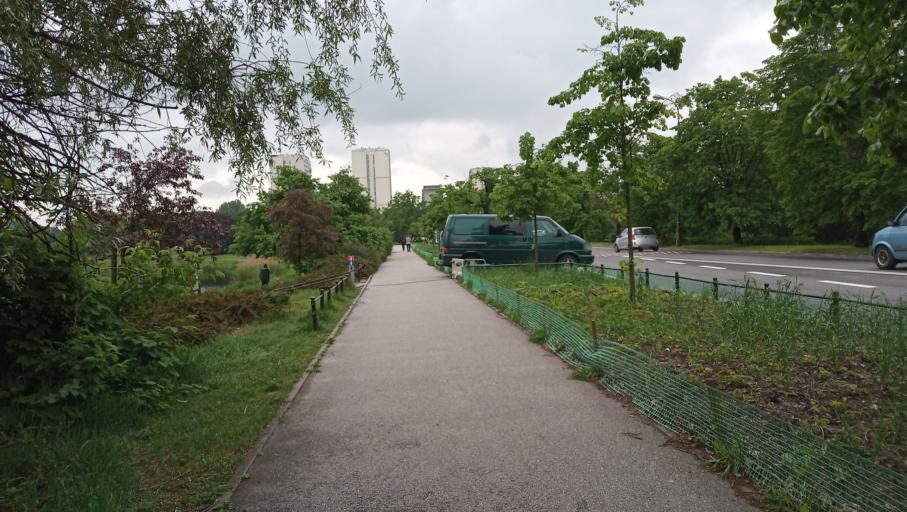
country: PL
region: Masovian Voivodeship
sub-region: Warszawa
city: Zoliborz
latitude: 52.2764
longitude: 20.9907
